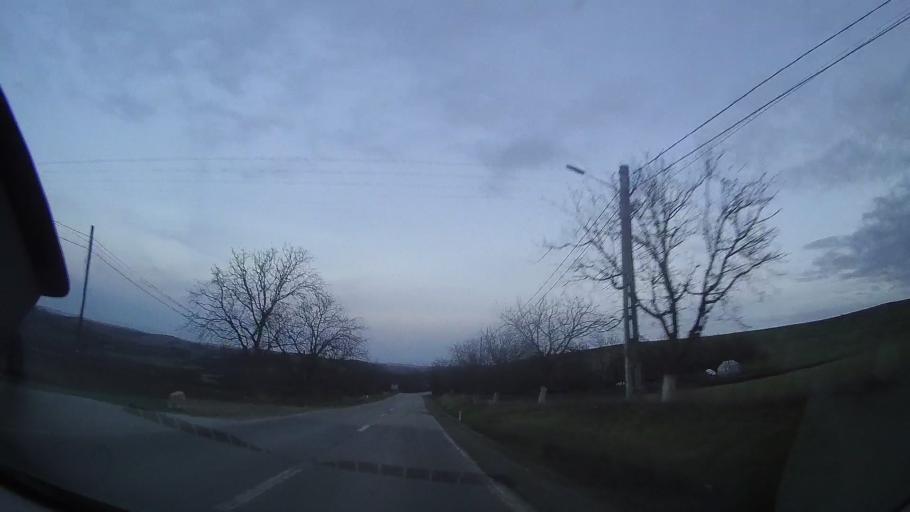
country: RO
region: Cluj
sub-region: Comuna Mociu
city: Mociu
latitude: 46.7978
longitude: 24.0050
